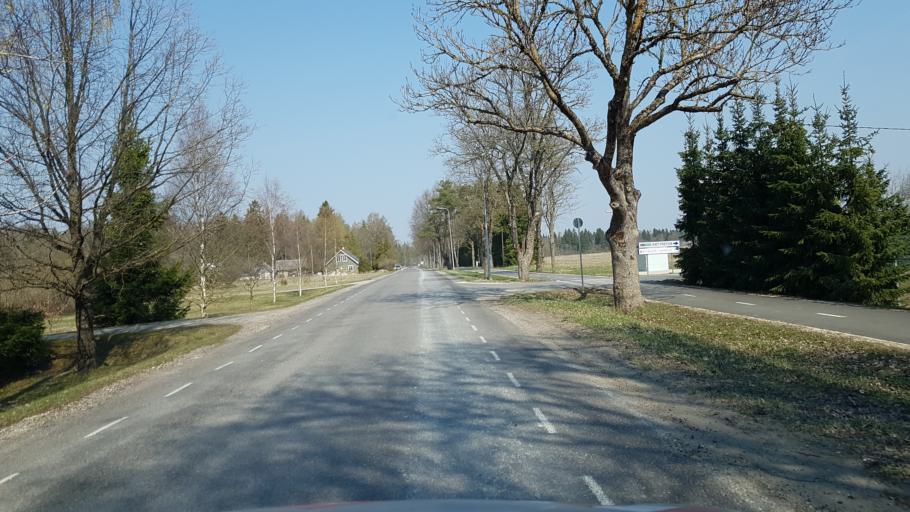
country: EE
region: Raplamaa
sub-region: Kohila vald
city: Kohila
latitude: 59.1624
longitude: 24.6511
